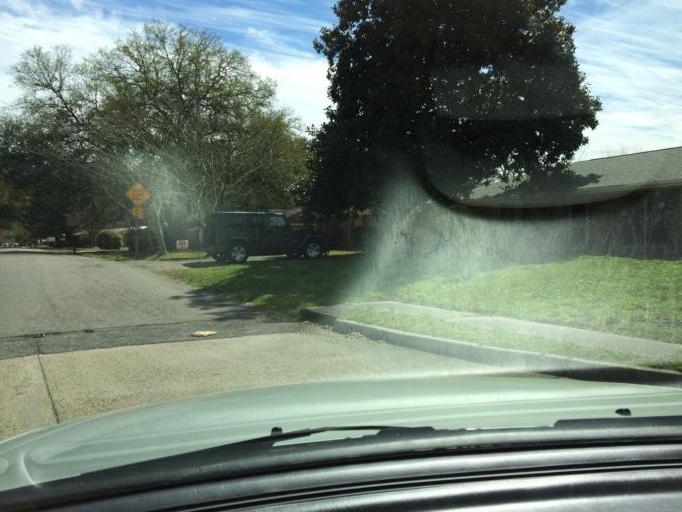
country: US
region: Louisiana
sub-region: Lafayette Parish
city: Lafayette
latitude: 30.2045
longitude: -92.0608
